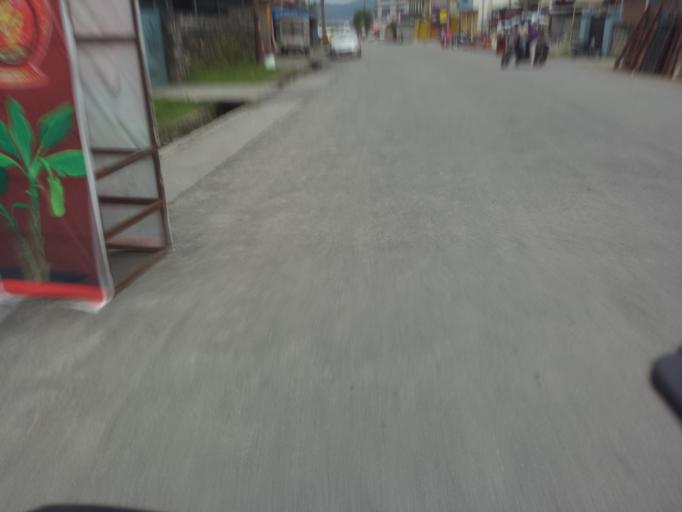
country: NP
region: Western Region
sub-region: Gandaki Zone
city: Pokhara
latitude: 28.2072
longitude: 83.9944
